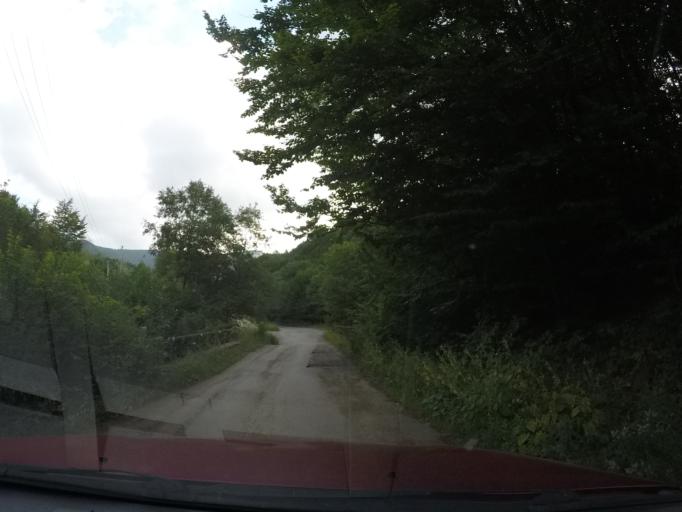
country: UA
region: Zakarpattia
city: Velykyi Bereznyi
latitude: 48.9504
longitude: 22.6613
